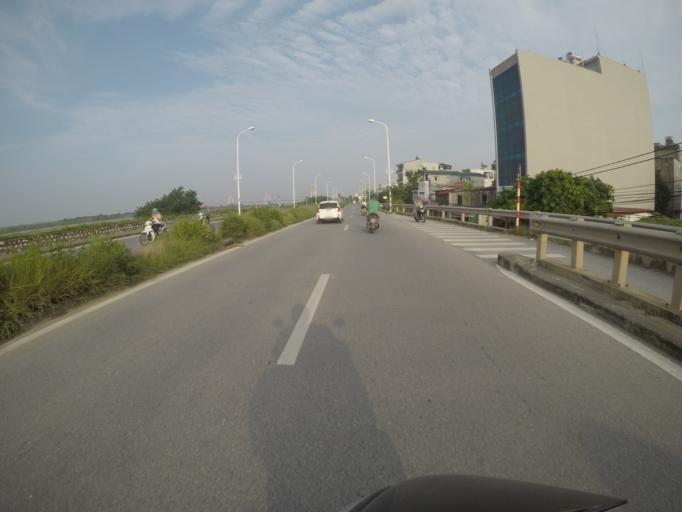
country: VN
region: Ha Noi
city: Tay Ho
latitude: 21.0898
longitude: 105.8053
